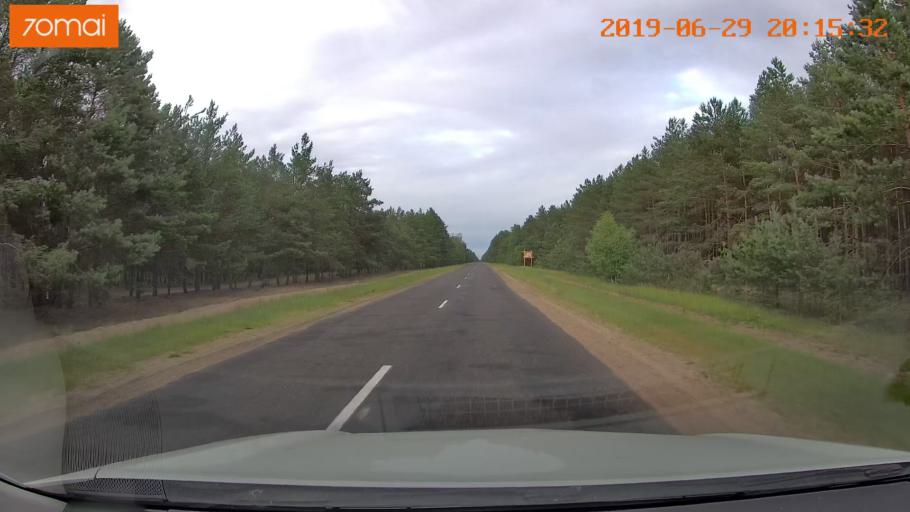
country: BY
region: Brest
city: Asnyezhytsy
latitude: 52.3749
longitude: 26.1779
